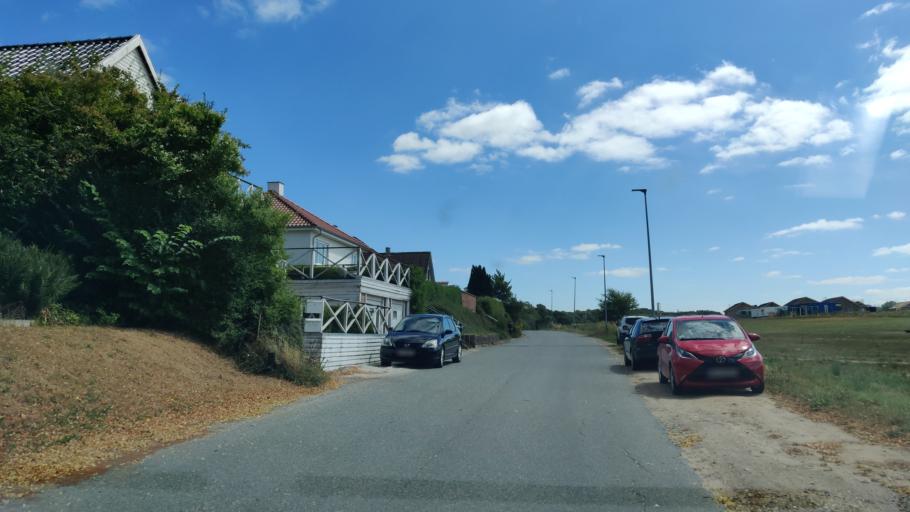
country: DK
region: South Denmark
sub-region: Fredericia Kommune
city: Taulov
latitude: 55.5259
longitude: 9.5430
